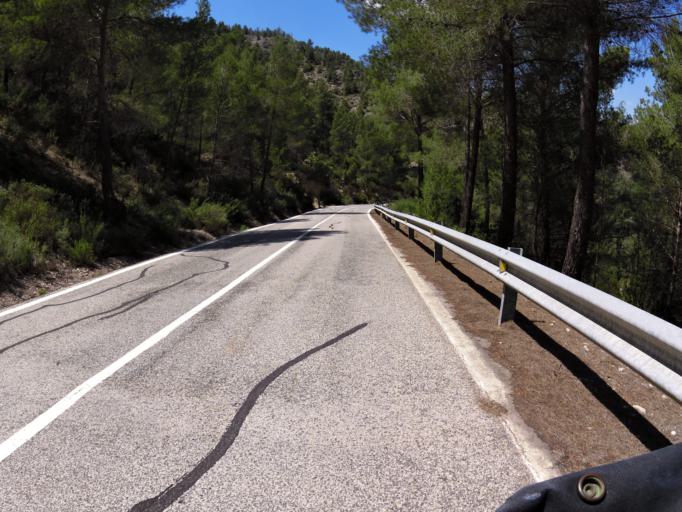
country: ES
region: Valencia
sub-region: Provincia de Valencia
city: Casas Bajas
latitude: 39.9884
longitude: -1.2768
